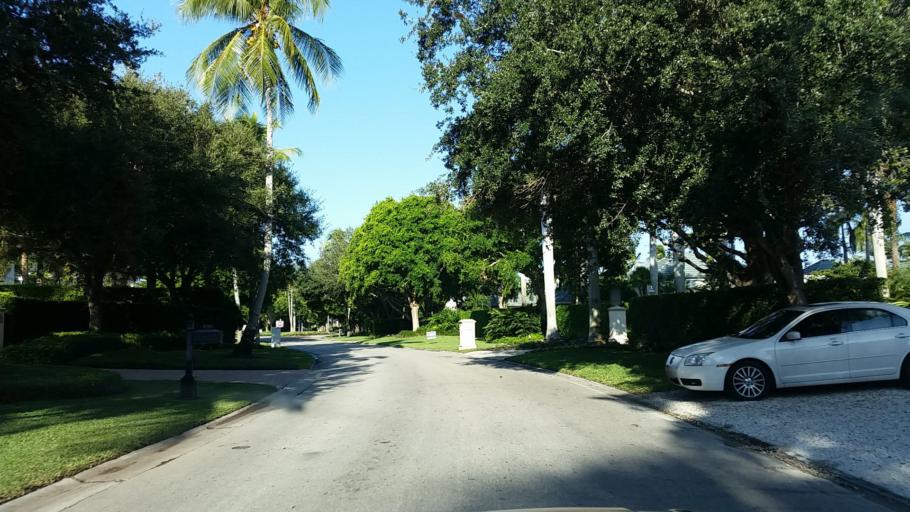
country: US
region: Florida
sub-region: Collier County
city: Naples
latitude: 26.1118
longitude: -81.7939
